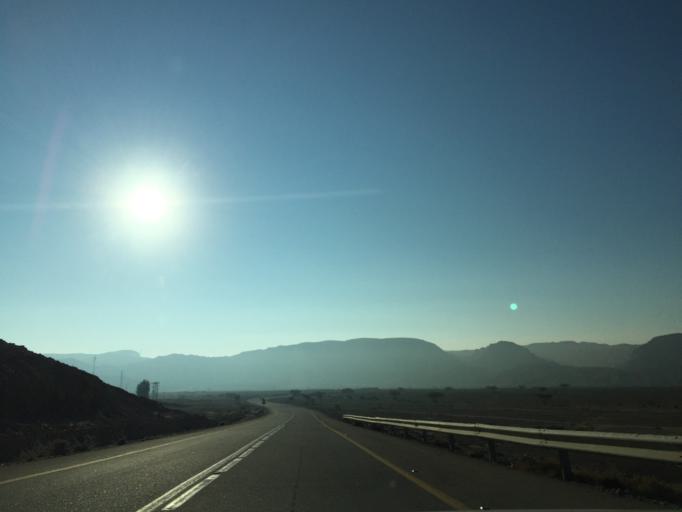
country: IL
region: Southern District
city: Mitzpe Ramon
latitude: 30.3348
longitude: 34.9497
